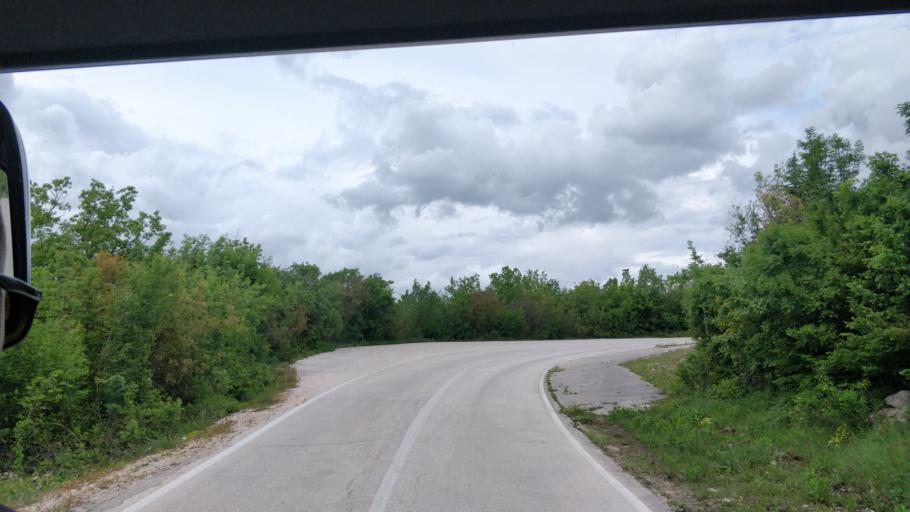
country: BA
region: Federation of Bosnia and Herzegovina
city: Ljubuski
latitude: 43.1792
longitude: 17.5098
